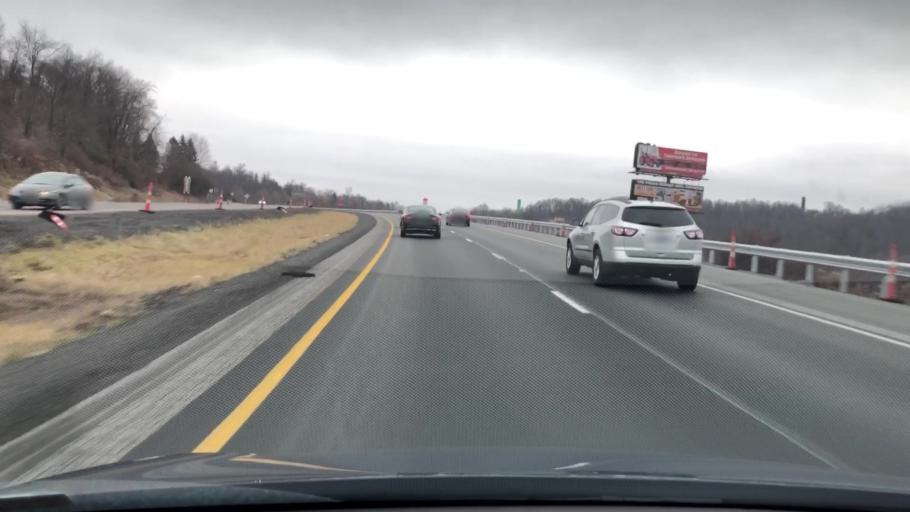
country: US
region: West Virginia
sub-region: Monongalia County
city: Star City
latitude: 39.6946
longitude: -80.0434
